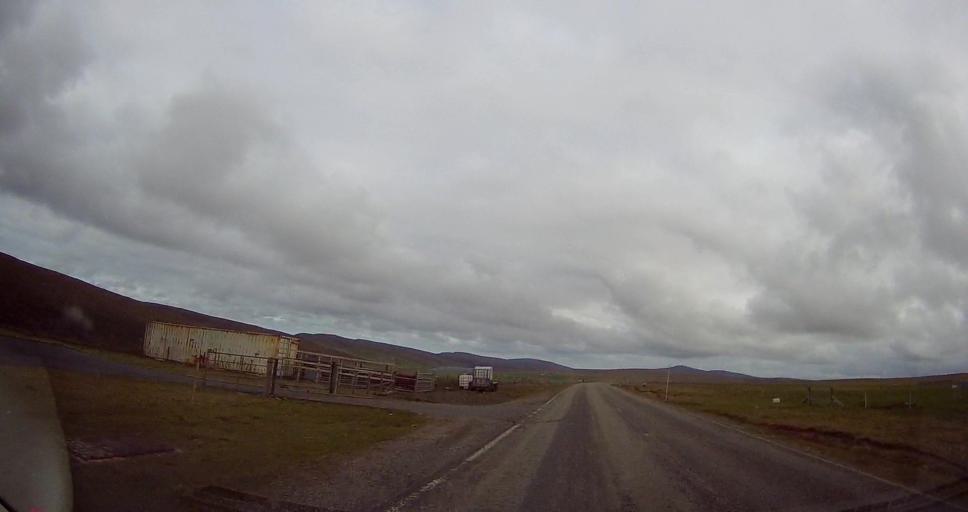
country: GB
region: Scotland
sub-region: Shetland Islands
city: Shetland
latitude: 60.7370
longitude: -0.8941
